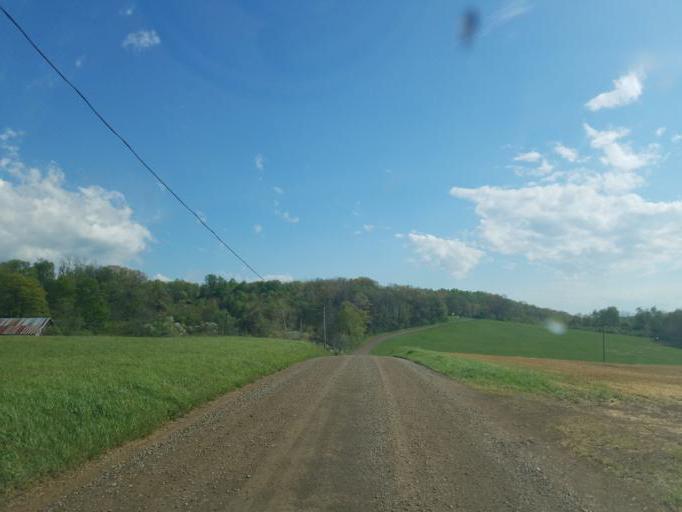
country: US
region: Ohio
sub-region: Knox County
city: Oak Hill
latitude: 40.3999
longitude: -82.2257
